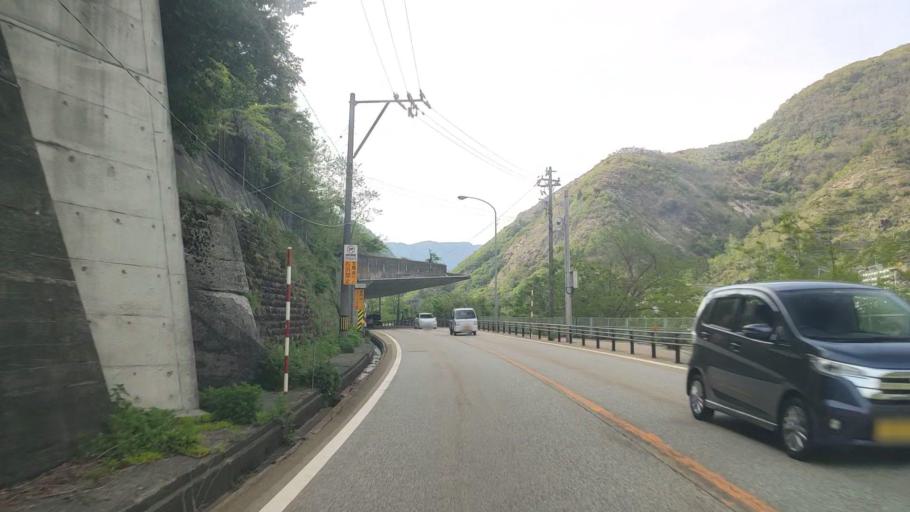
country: JP
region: Gifu
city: Takayama
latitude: 36.3471
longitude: 137.2938
